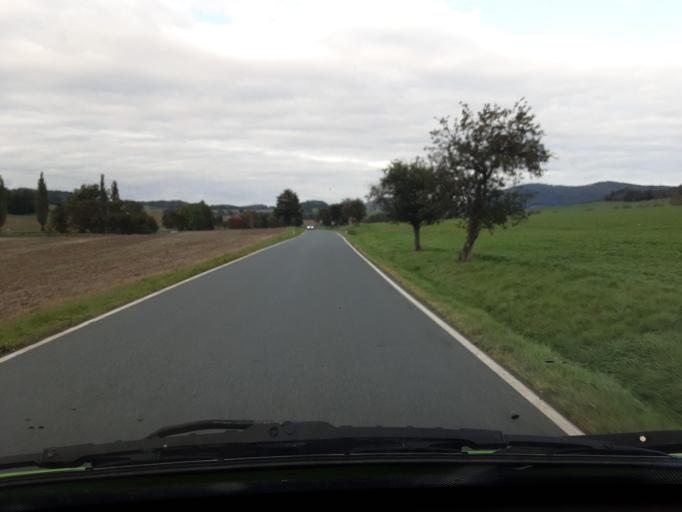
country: CZ
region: Plzensky
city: Janovice nad Uhlavou
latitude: 49.4015
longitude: 13.1502
